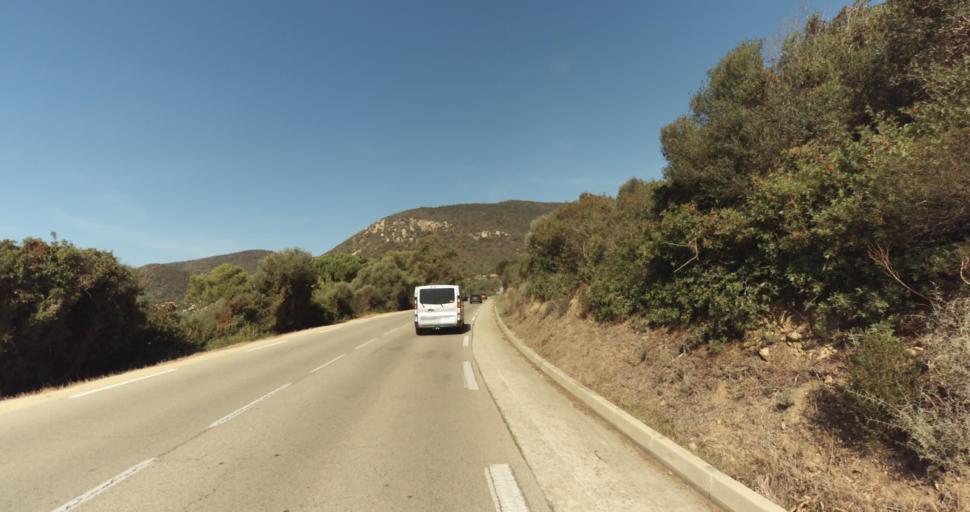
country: FR
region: Corsica
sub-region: Departement de la Corse-du-Sud
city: Ajaccio
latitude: 41.9096
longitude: 8.6494
